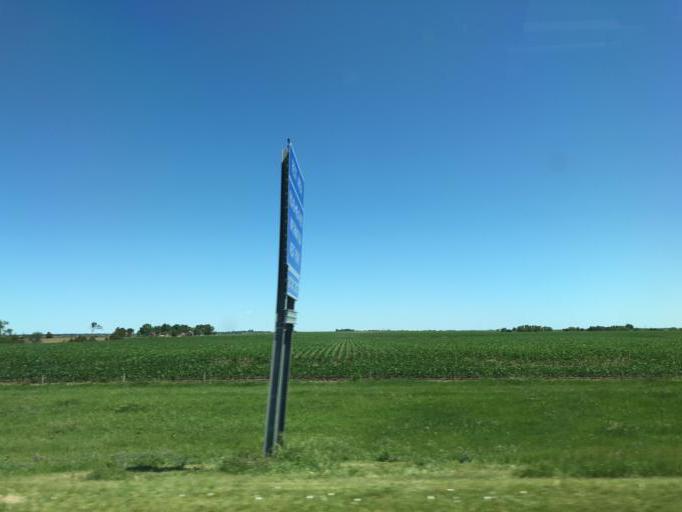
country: US
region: Nebraska
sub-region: York County
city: York
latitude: 40.8222
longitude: -97.5465
